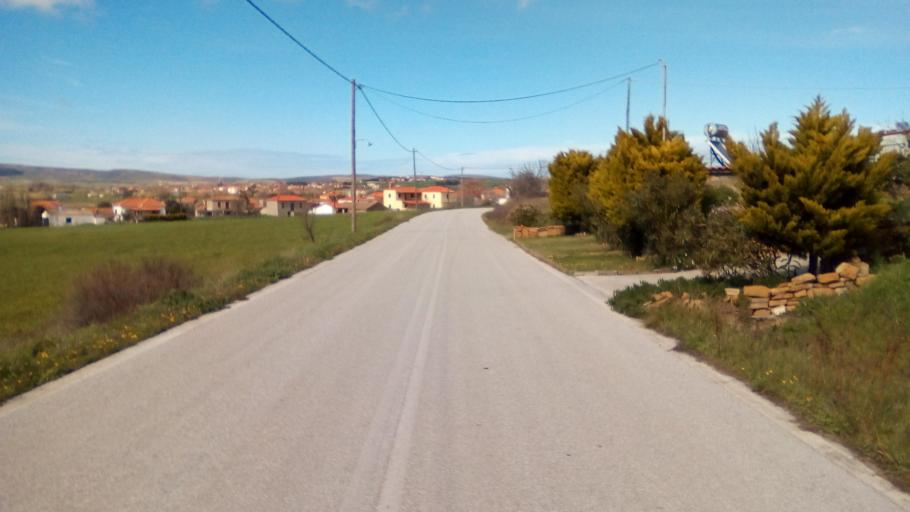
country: GR
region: North Aegean
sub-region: Nomos Lesvou
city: Myrina
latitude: 39.9313
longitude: 25.2310
